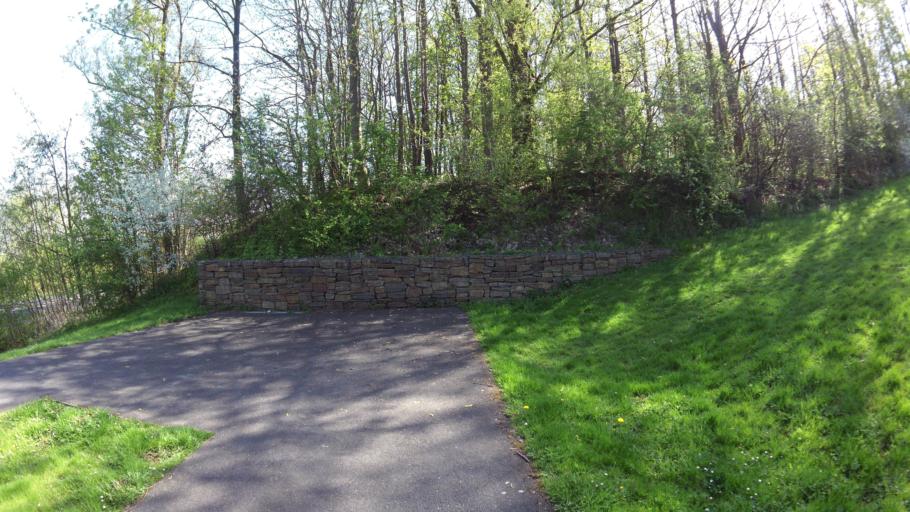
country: DE
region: North Rhine-Westphalia
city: Baesweiler
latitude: 50.9114
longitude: 6.1647
